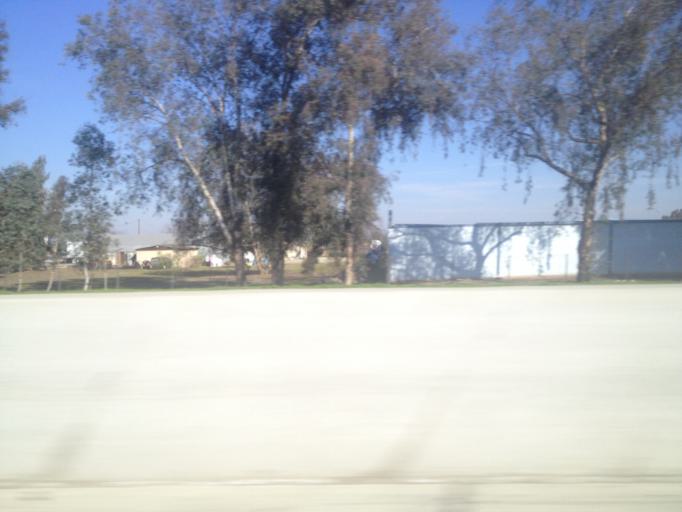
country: US
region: California
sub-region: Fresno County
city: Kingsburg
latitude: 36.5214
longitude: -119.5659
